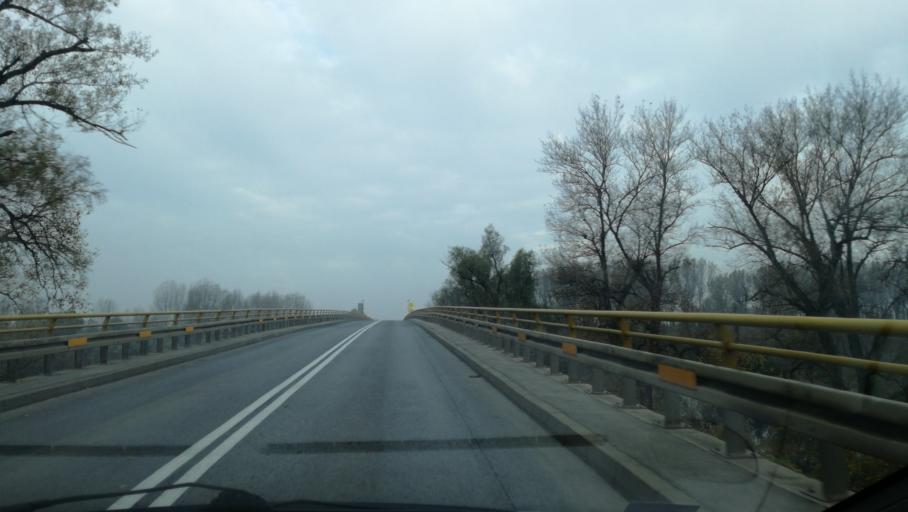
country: RS
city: Taras
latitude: 45.3970
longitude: 20.2138
